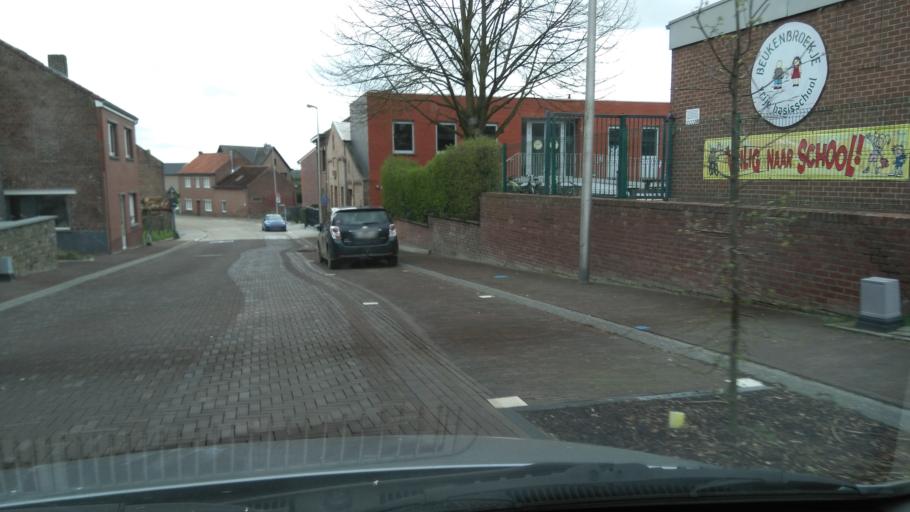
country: BE
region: Flanders
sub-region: Provincie Limburg
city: Riemst
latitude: 50.8456
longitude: 5.5751
